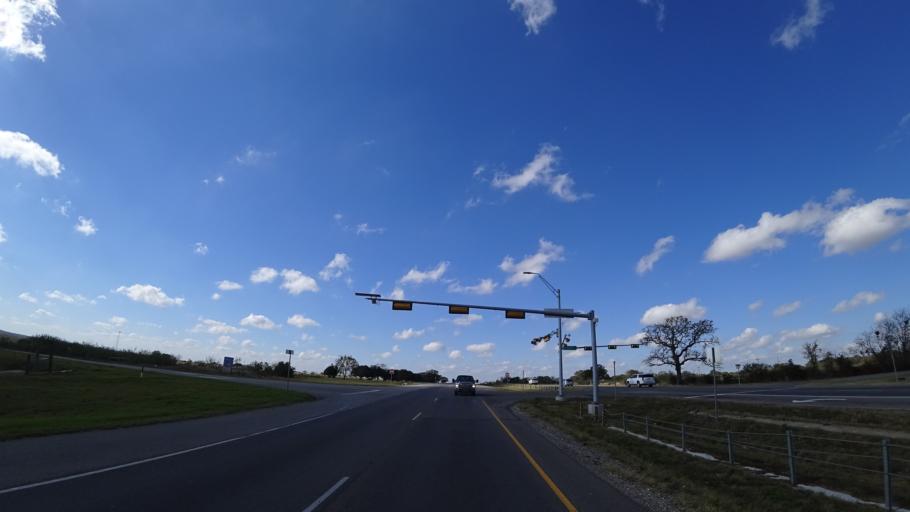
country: US
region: Texas
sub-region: Travis County
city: Garfield
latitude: 30.1876
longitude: -97.5976
